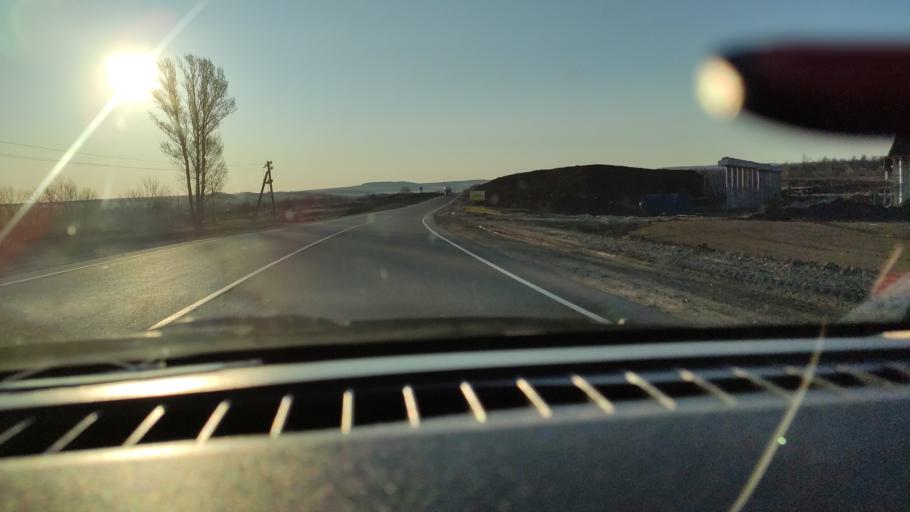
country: RU
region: Saratov
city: Sennoy
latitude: 52.1608
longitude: 47.0532
